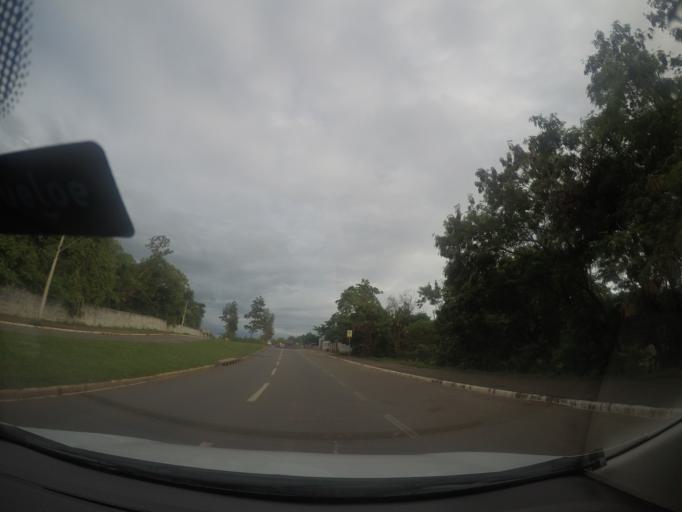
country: BR
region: Goias
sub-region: Goiania
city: Goiania
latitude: -16.6177
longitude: -49.3390
